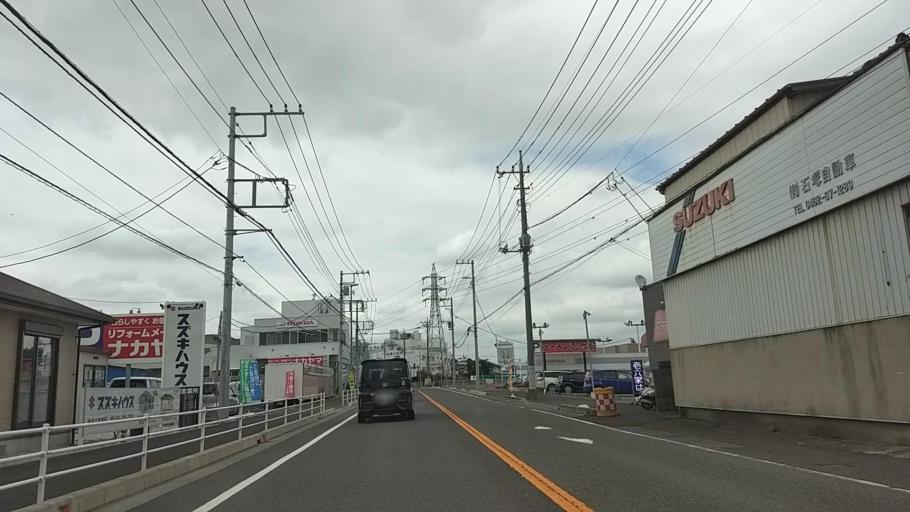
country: JP
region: Kanagawa
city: Minami-rinkan
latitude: 35.4294
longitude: 139.4680
